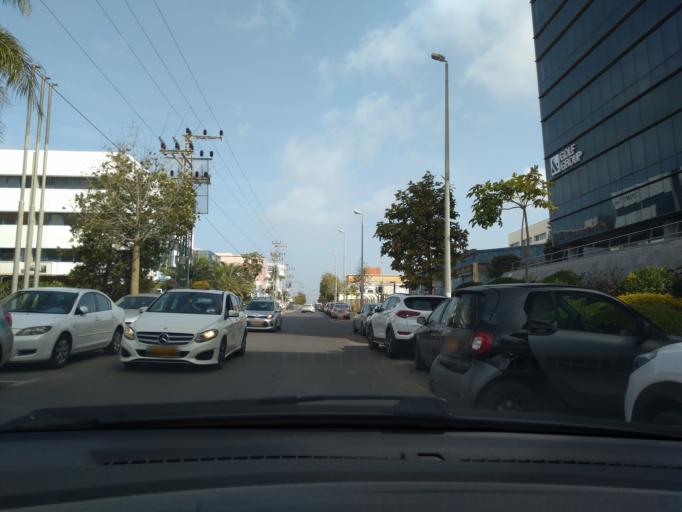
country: IL
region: Central District
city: Even Yehuda
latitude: 32.2774
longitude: 34.8583
